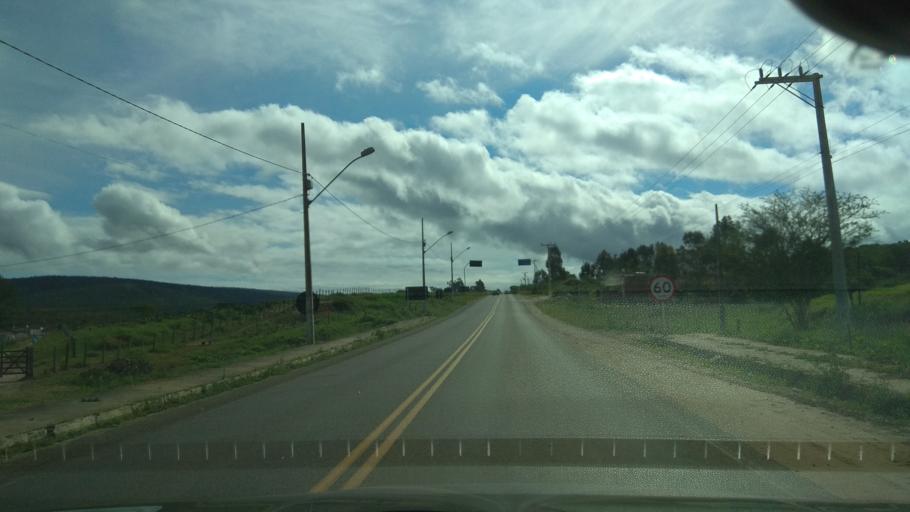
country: BR
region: Bahia
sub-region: Jaguaquara
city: Jaguaquara
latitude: -13.4458
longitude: -39.9364
